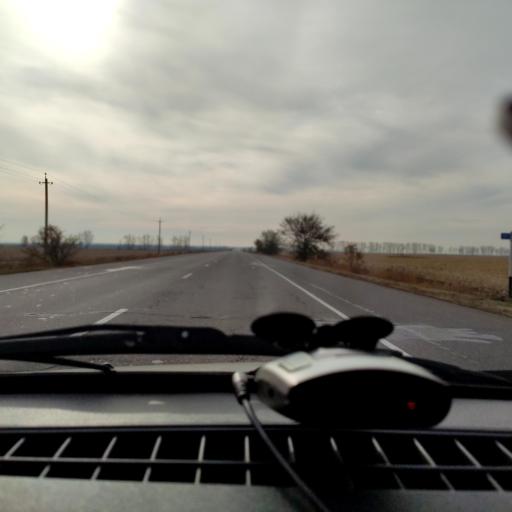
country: RU
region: Voronezj
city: Strelitsa
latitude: 51.5390
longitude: 38.9704
